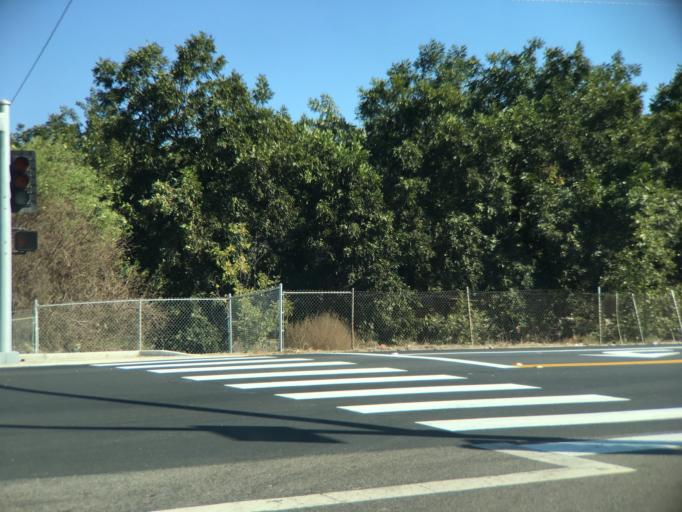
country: US
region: California
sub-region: San Diego County
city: Valley Center
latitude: 33.2686
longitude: -116.9540
